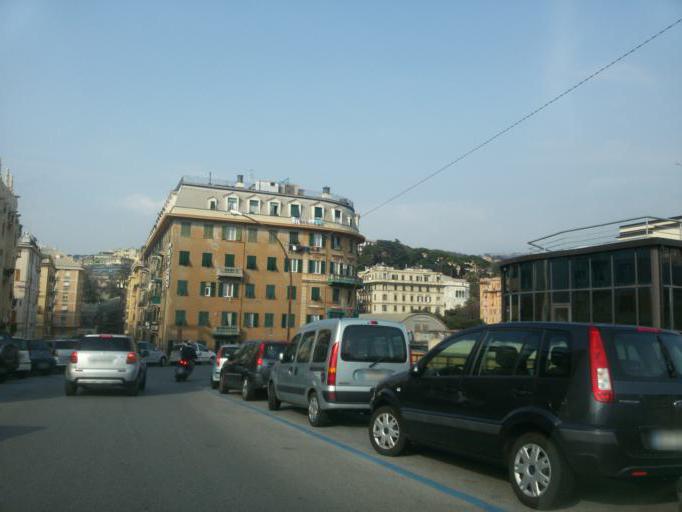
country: IT
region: Liguria
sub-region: Provincia di Genova
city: Genoa
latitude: 44.4058
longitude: 8.9592
